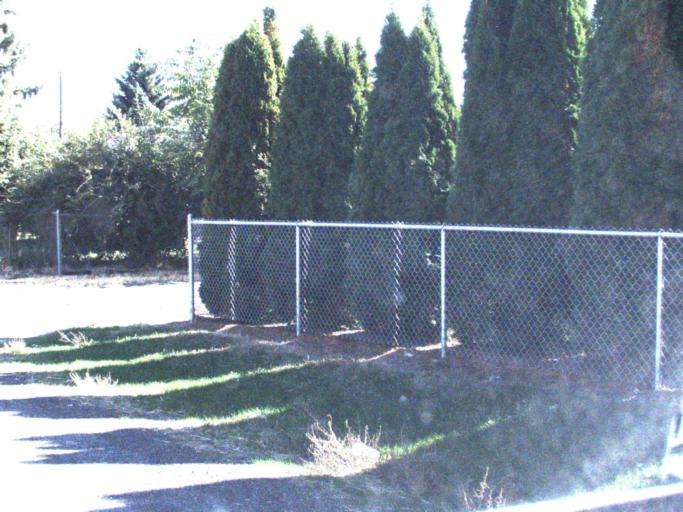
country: US
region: Washington
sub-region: Walla Walla County
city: Waitsburg
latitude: 46.2702
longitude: -118.1595
